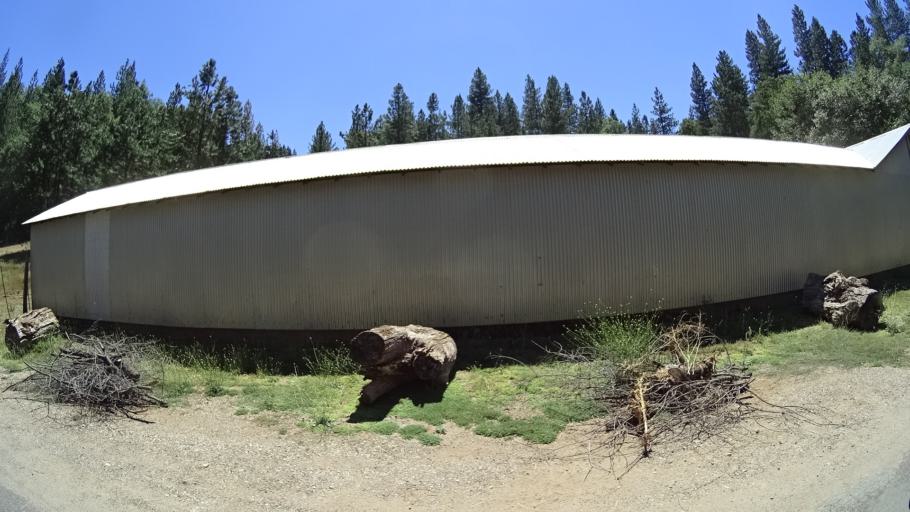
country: US
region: California
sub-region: Calaveras County
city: Mountain Ranch
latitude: 38.2765
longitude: -120.4566
